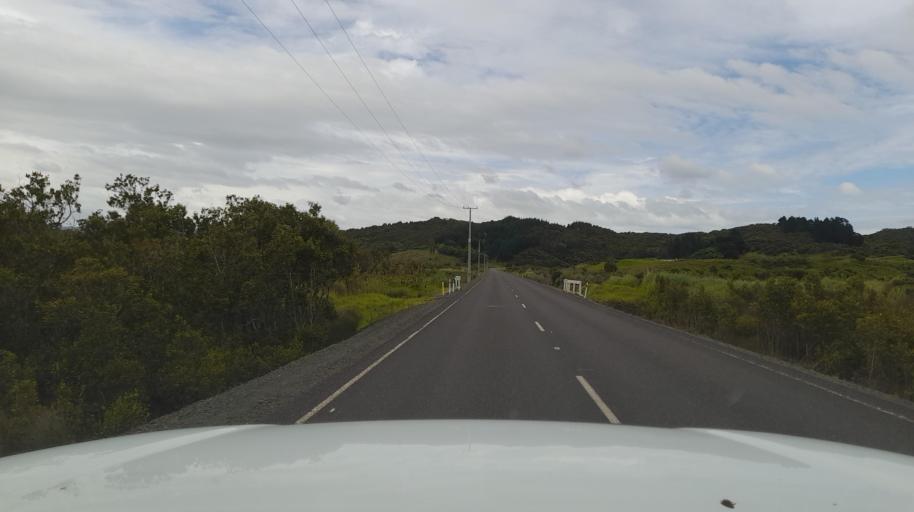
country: NZ
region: Northland
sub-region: Far North District
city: Kaitaia
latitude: -35.4012
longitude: 173.3819
